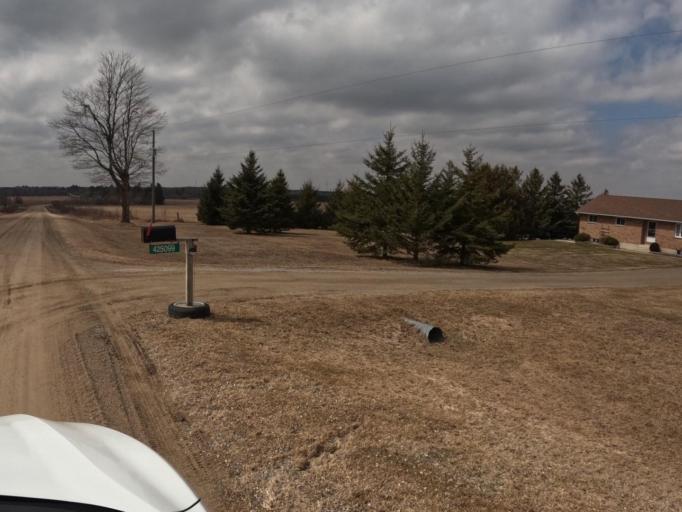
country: CA
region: Ontario
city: Shelburne
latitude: 44.0365
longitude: -80.2158
